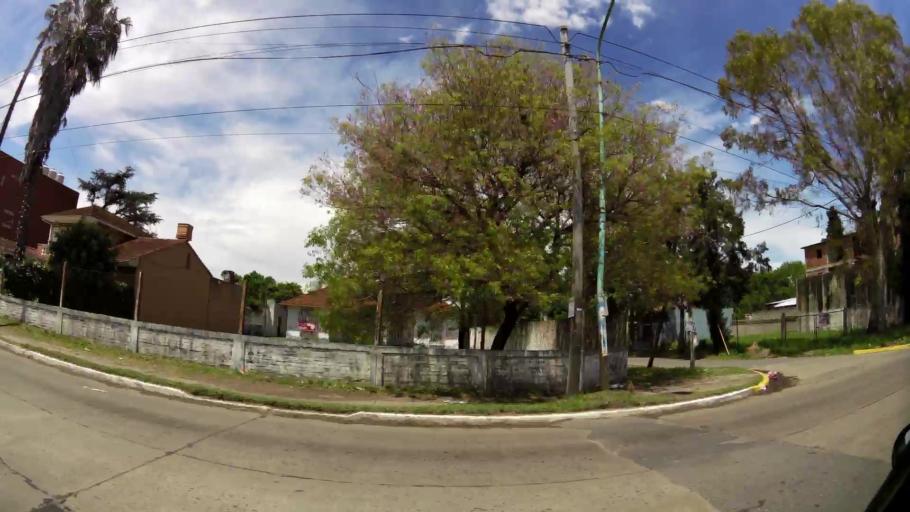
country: AR
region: Buenos Aires
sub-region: Partido de Quilmes
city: Quilmes
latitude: -34.7864
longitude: -58.2728
